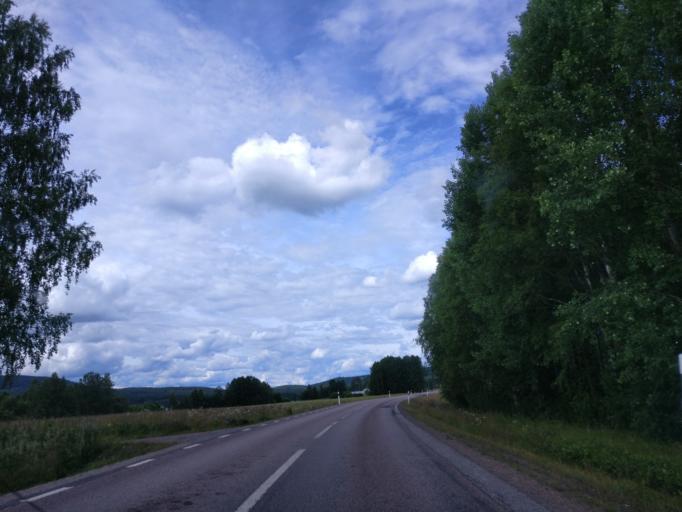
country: SE
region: Vaermland
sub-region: Hagfors Kommun
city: Ekshaerad
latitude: 60.1546
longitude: 13.4243
